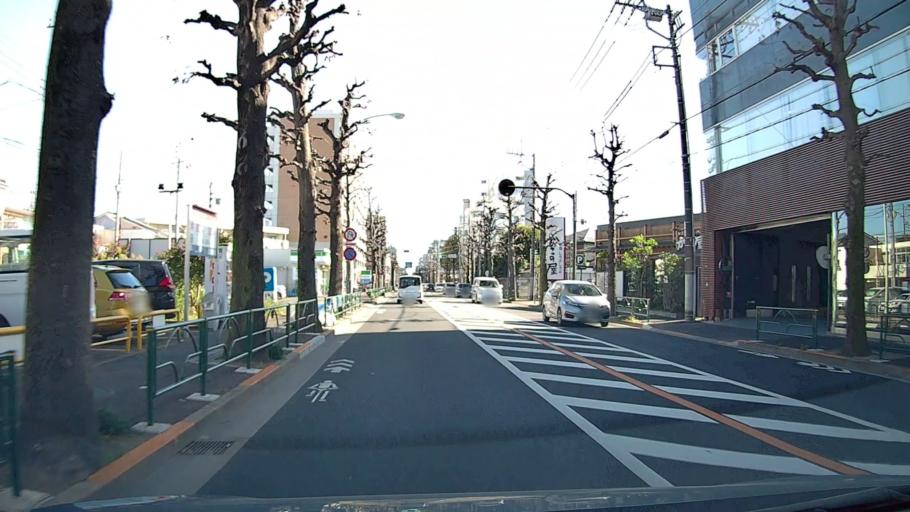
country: JP
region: Saitama
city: Wako
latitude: 35.7272
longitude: 139.6333
